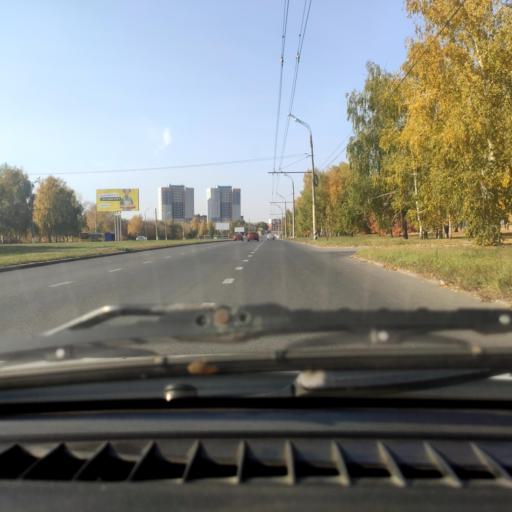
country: RU
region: Samara
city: Tol'yatti
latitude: 53.5032
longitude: 49.2609
